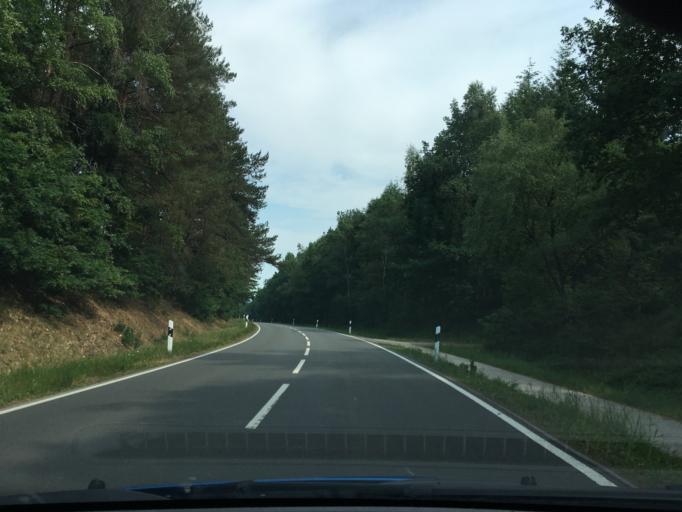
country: DE
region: Lower Saxony
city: Asendorf
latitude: 53.2671
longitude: 9.9631
